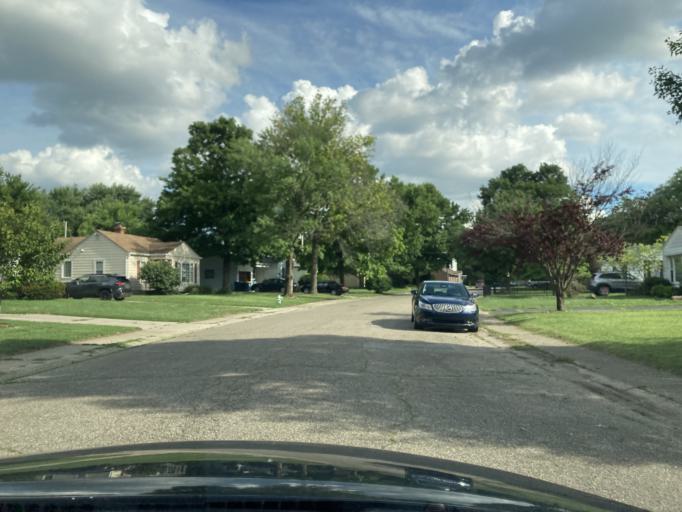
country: US
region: Indiana
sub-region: Marion County
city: Broad Ripple
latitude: 39.8488
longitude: -86.1292
